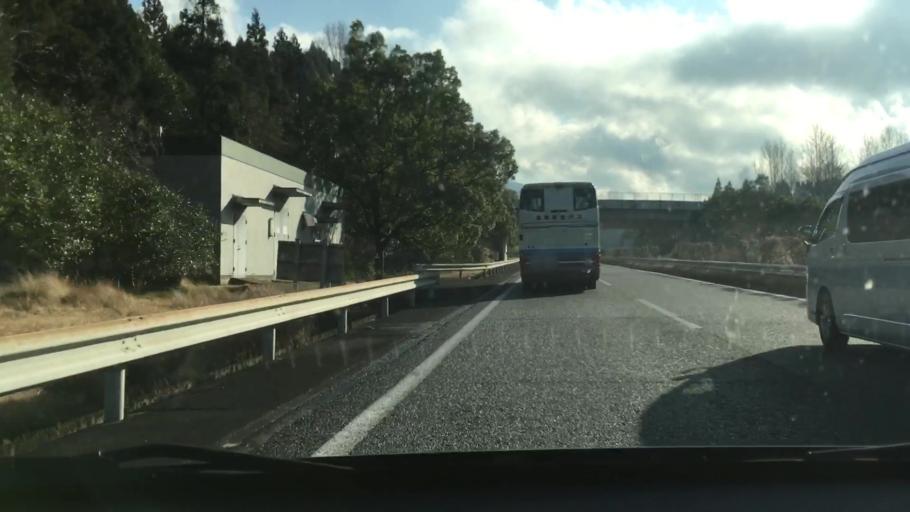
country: JP
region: Kagoshima
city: Okuchi-shinohara
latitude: 32.0342
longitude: 130.7985
